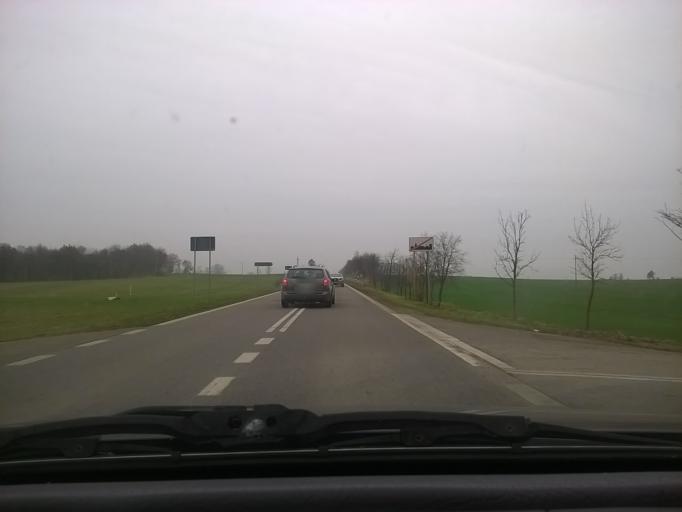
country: PL
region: Warmian-Masurian Voivodeship
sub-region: Powiat ketrzynski
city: Ketrzyn
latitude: 54.1291
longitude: 21.2731
